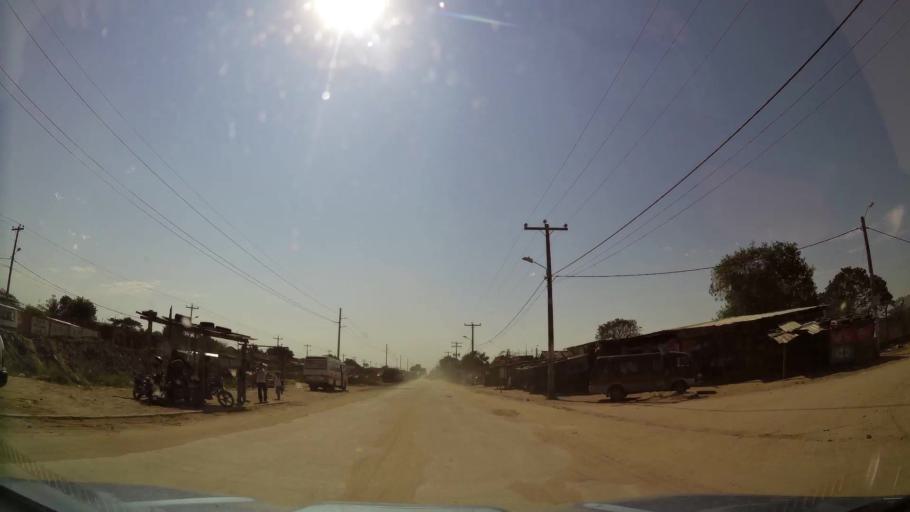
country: BO
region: Santa Cruz
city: Cotoca
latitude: -17.7488
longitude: -63.0948
